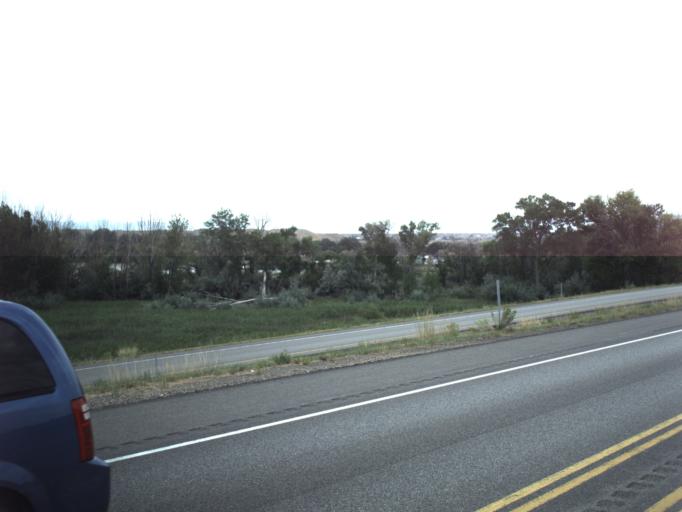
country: US
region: Utah
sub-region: Carbon County
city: Price
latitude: 39.5874
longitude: -110.8107
